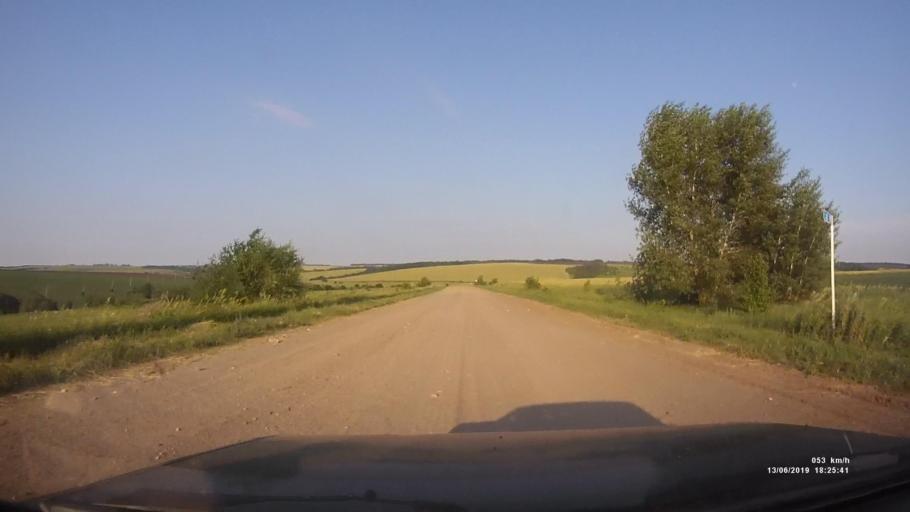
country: RU
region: Rostov
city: Kazanskaya
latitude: 49.8511
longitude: 41.3050
